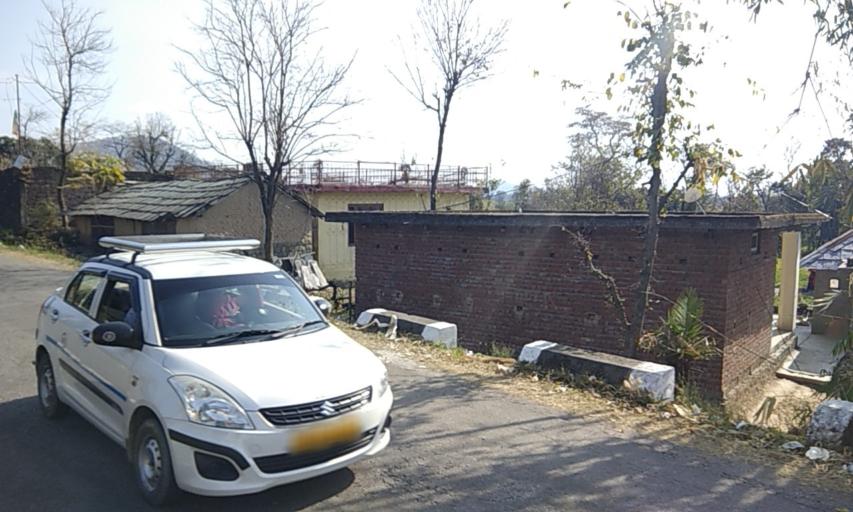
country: IN
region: Himachal Pradesh
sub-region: Kangra
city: Dharmsala
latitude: 32.1565
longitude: 76.4139
